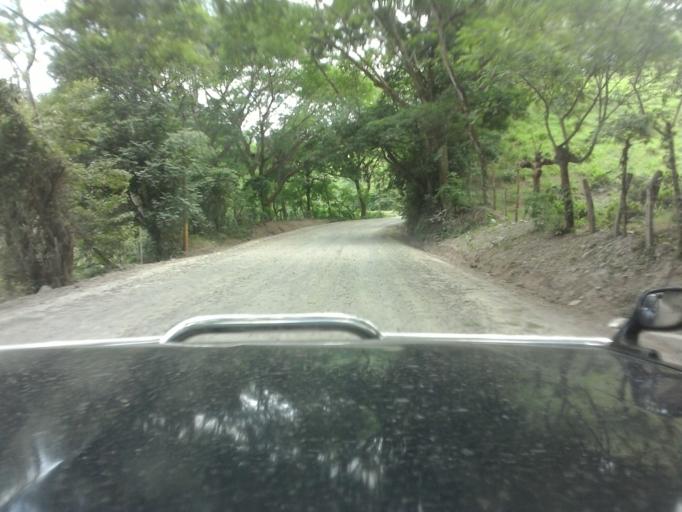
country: CR
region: Guanacaste
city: Juntas
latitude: 10.2215
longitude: -84.8540
